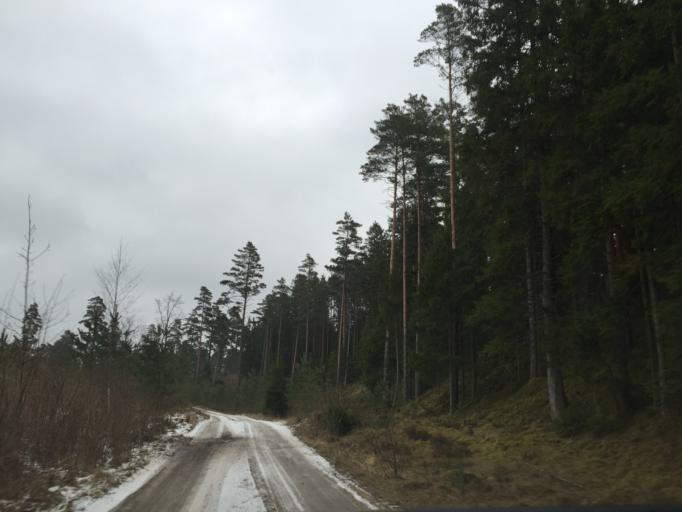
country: EE
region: Saare
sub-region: Kuressaare linn
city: Kuressaare
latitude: 58.3803
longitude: 22.2510
